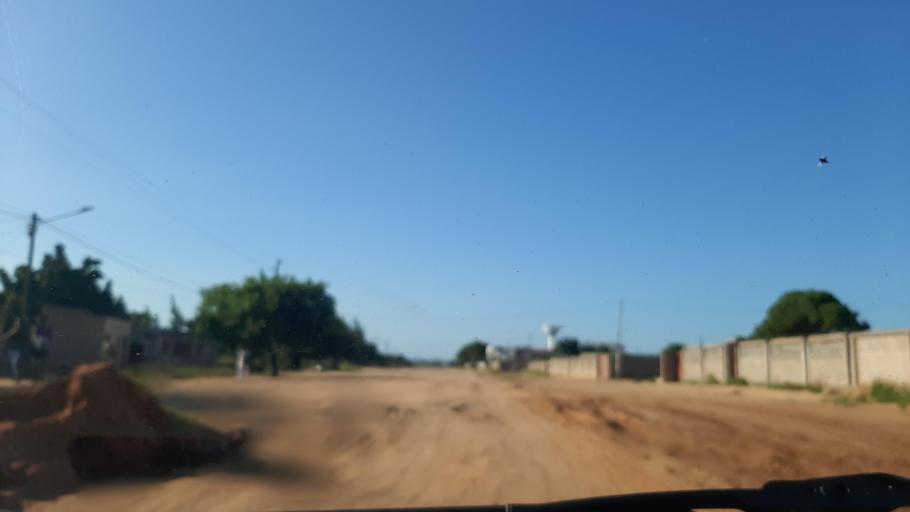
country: MZ
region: Maputo City
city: Maputo
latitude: -25.7929
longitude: 32.5522
